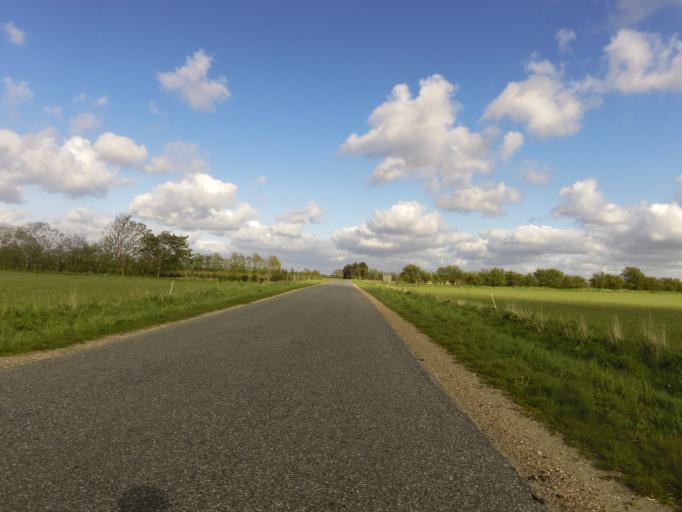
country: DK
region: South Denmark
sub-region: Esbjerg Kommune
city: Ribe
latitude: 55.2588
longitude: 8.7909
